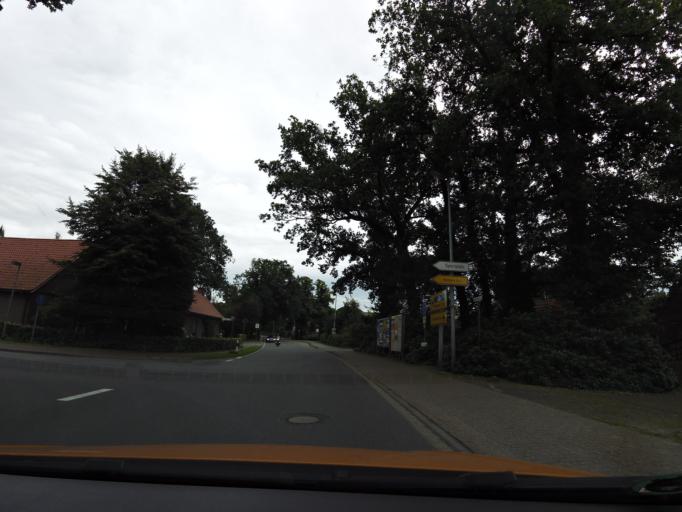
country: DE
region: Lower Saxony
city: Wiefelstede
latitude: 53.1993
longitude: 8.1245
